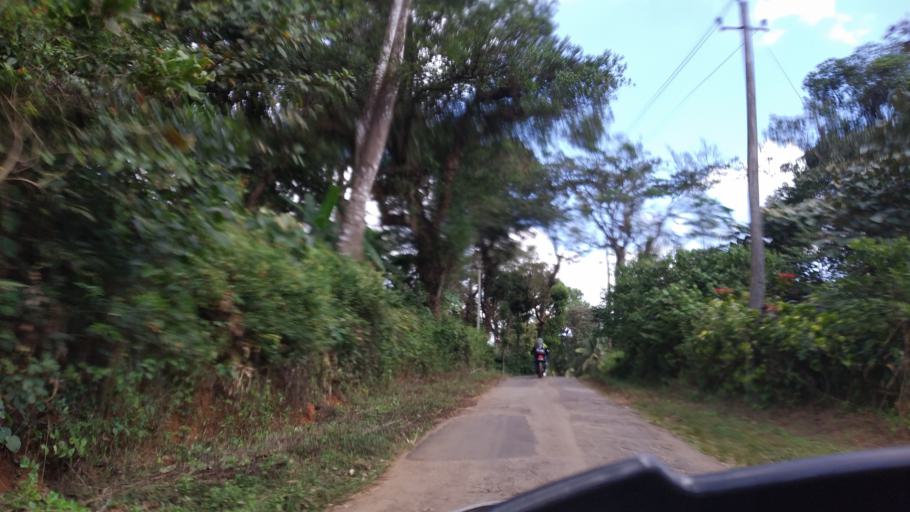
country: IN
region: Karnataka
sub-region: Kodagu
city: Ponnampet
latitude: 12.0344
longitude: 75.9119
